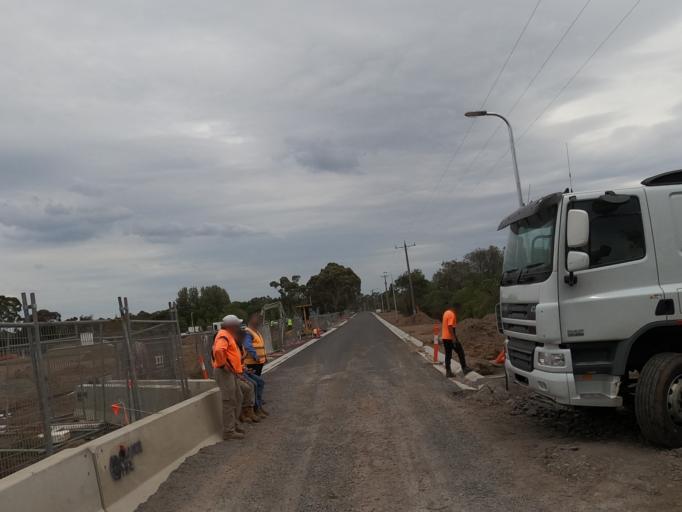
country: AU
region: Victoria
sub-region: Hume
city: Greenvale
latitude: -37.6415
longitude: 144.8714
